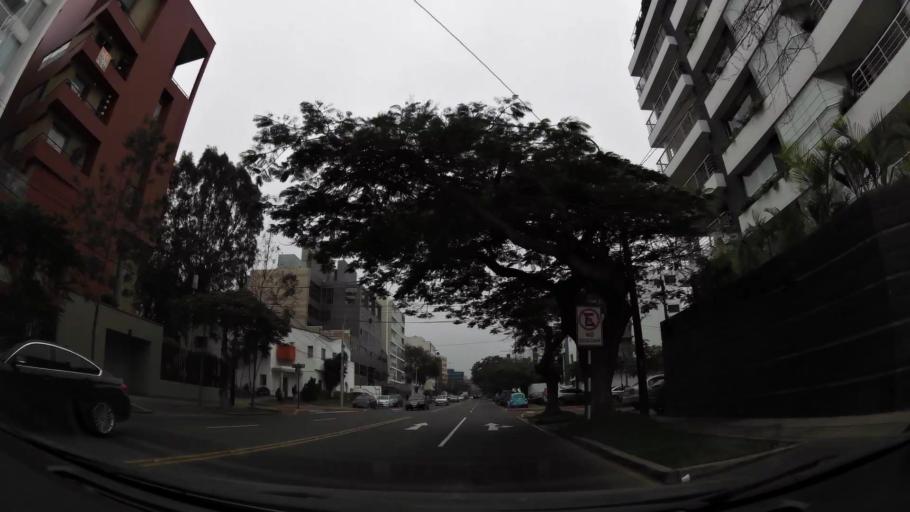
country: PE
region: Lima
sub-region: Lima
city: San Isidro
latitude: -12.0955
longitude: -77.0419
